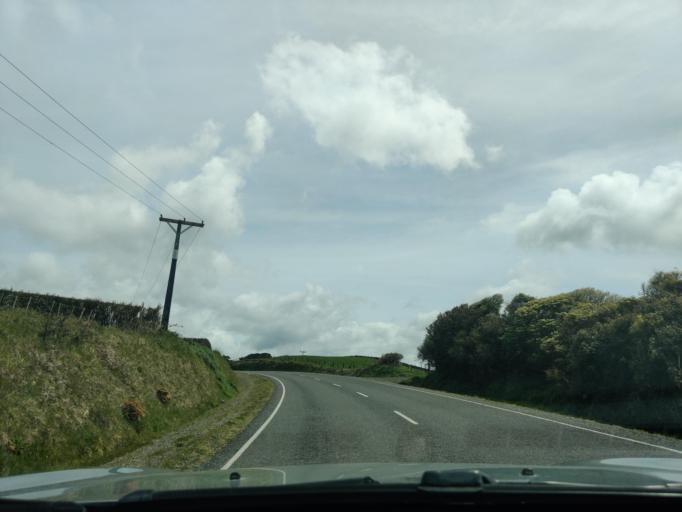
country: NZ
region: Taranaki
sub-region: South Taranaki District
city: Eltham
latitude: -39.3762
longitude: 174.1671
